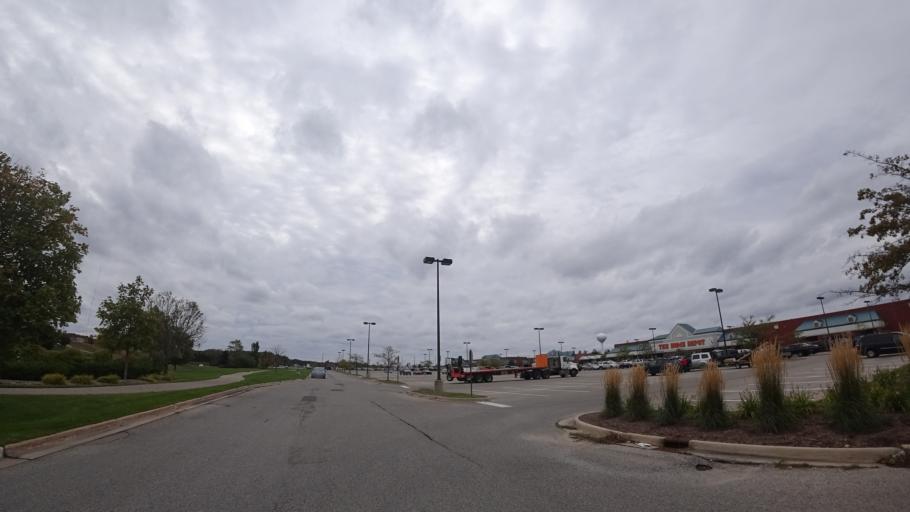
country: US
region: Michigan
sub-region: Emmet County
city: Petoskey
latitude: 45.3528
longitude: -84.9717
